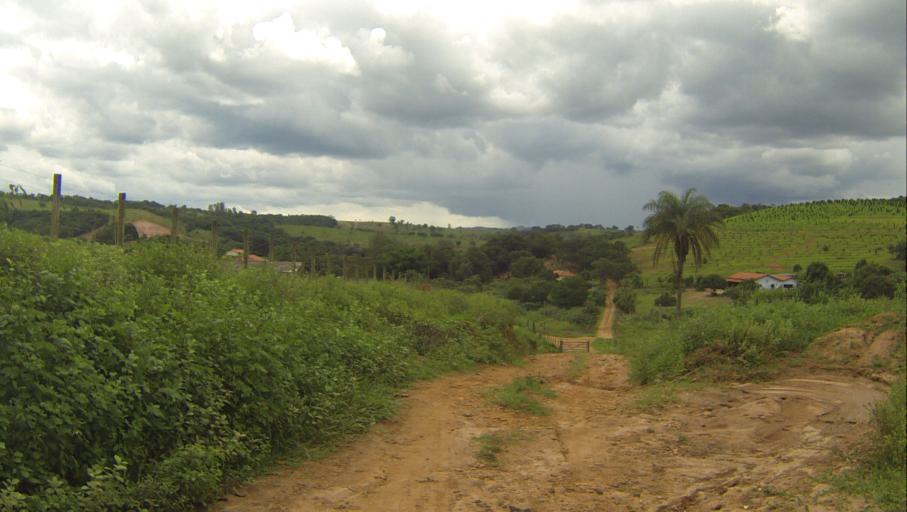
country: BR
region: Minas Gerais
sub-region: Brumadinho
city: Brumadinho
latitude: -20.1546
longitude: -44.1249
